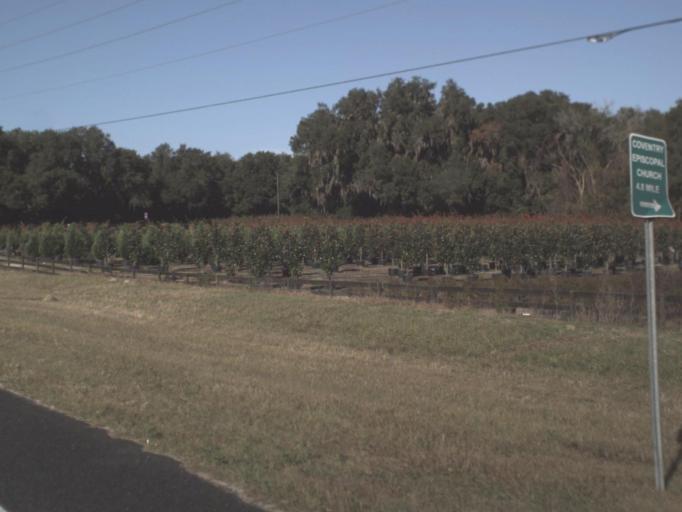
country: US
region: Florida
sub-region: Marion County
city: Belleview
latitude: 29.0261
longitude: -82.1186
